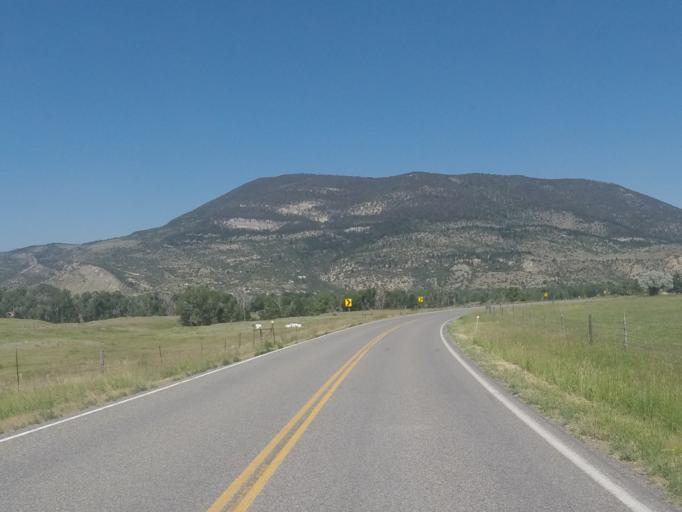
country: US
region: Montana
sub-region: Park County
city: Livingston
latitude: 45.5718
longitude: -110.5656
